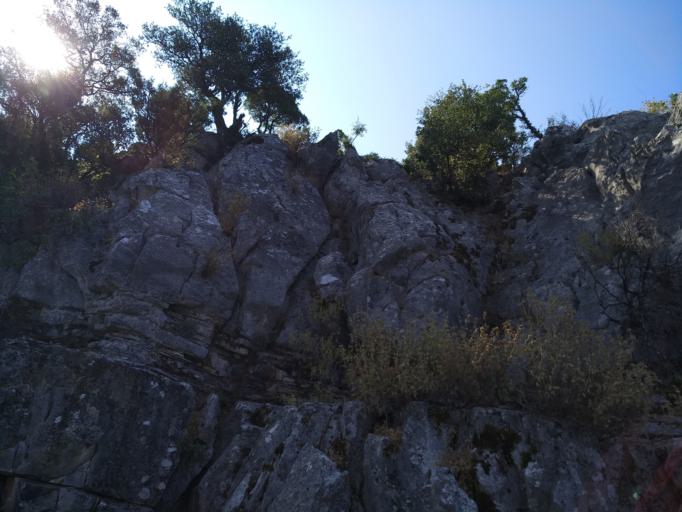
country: TR
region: Mugla
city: OEluedeniz
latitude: 36.5333
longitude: 29.1416
